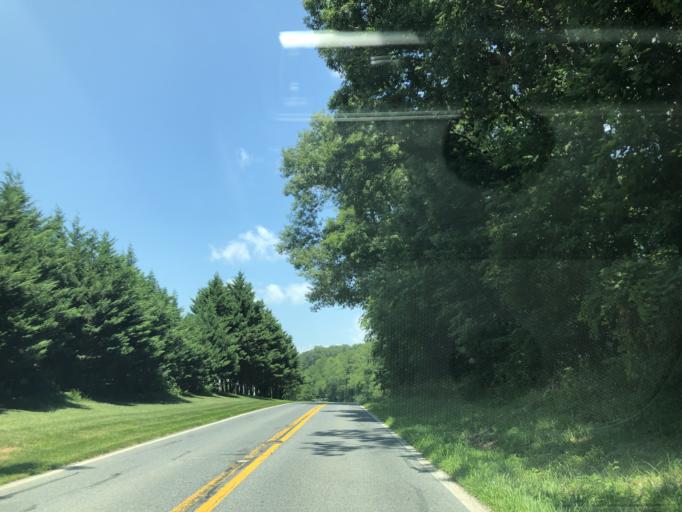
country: US
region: Maryland
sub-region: Carroll County
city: Westminster
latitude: 39.5230
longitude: -76.9496
